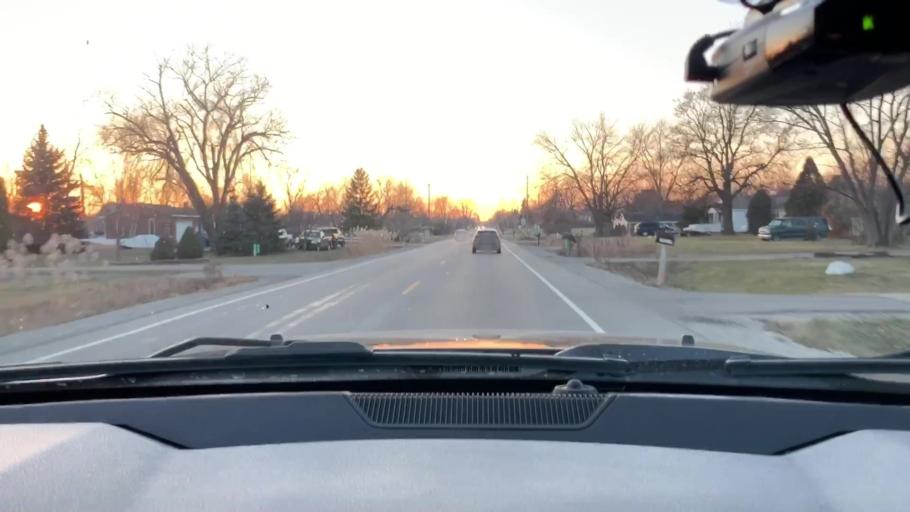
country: US
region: Michigan
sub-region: Wayne County
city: Flat Rock
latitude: 42.1236
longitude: -83.2822
